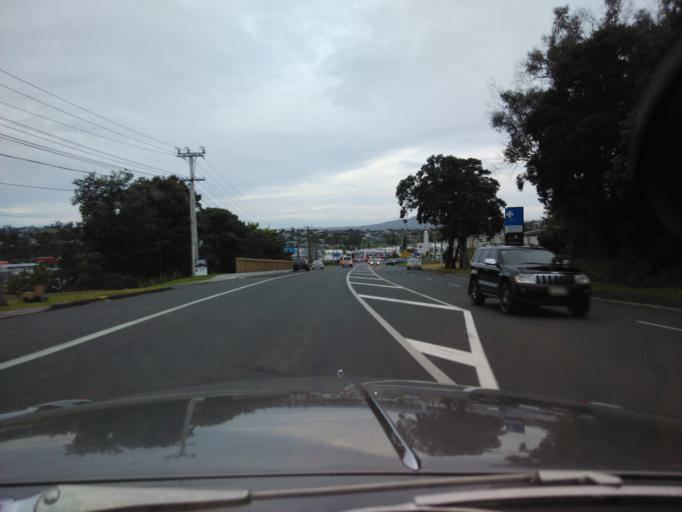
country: NZ
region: Auckland
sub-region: Auckland
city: North Shore
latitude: -36.7696
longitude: 174.7331
